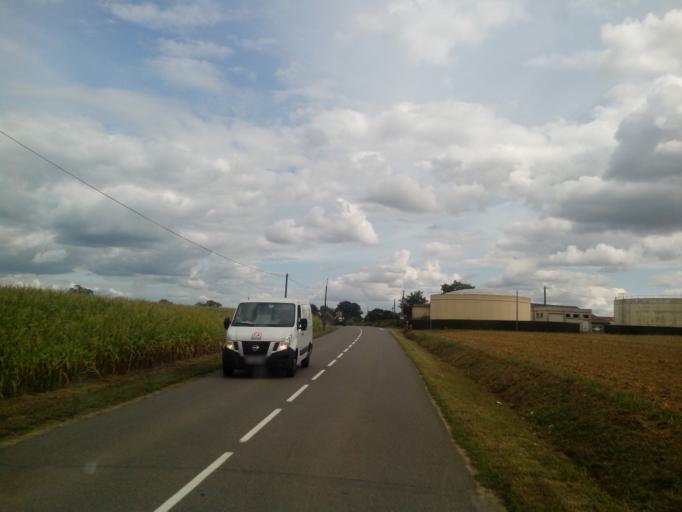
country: FR
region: Brittany
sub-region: Departement d'Ille-et-Vilaine
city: Melesse
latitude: 48.1974
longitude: -1.7097
